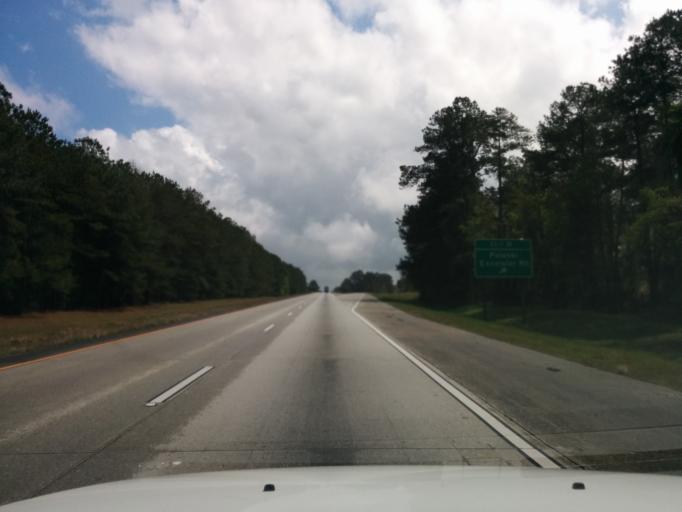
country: US
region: Georgia
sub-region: Candler County
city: Metter
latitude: 32.3407
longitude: -81.9587
